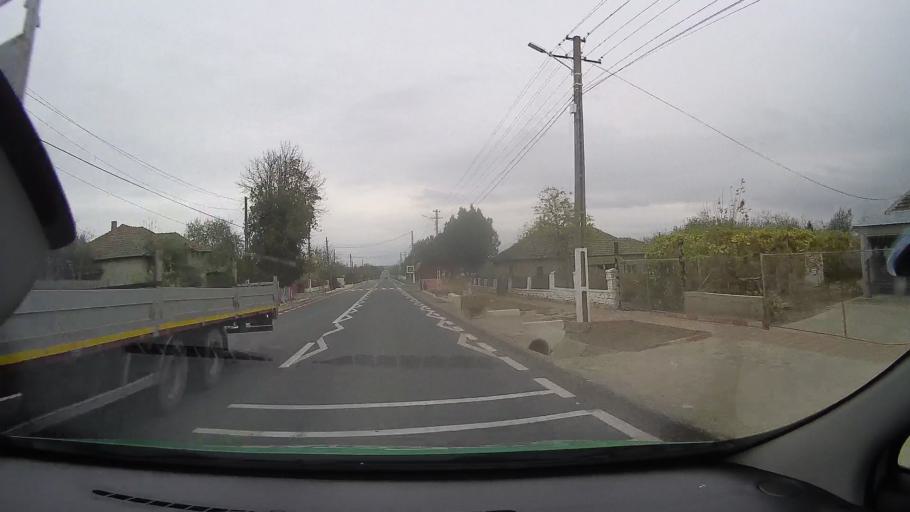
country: RO
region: Constanta
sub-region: Comuna Nicolae Balcescu
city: Nicolae Balcescu
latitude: 44.3892
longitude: 28.3720
